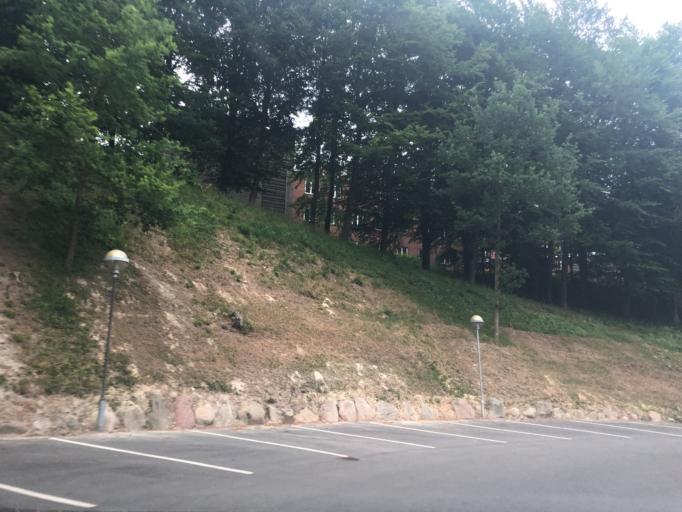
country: DK
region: South Denmark
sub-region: Kolding Kommune
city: Sonder Bjert
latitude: 55.4988
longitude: 9.5556
